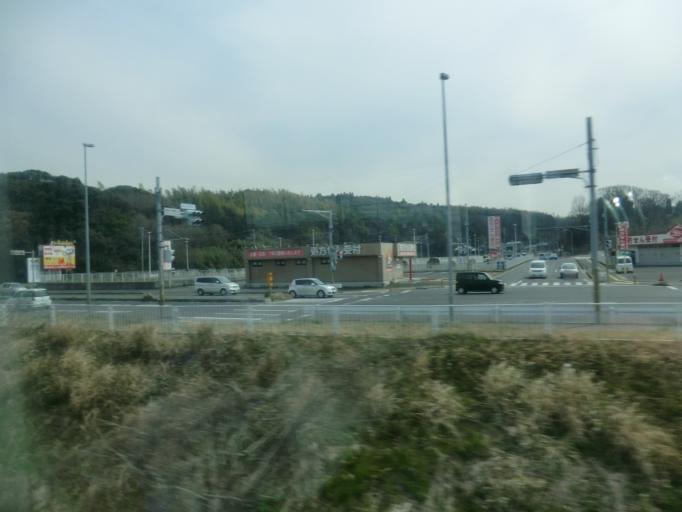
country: JP
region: Chiba
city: Kisarazu
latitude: 35.3622
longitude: 139.9219
